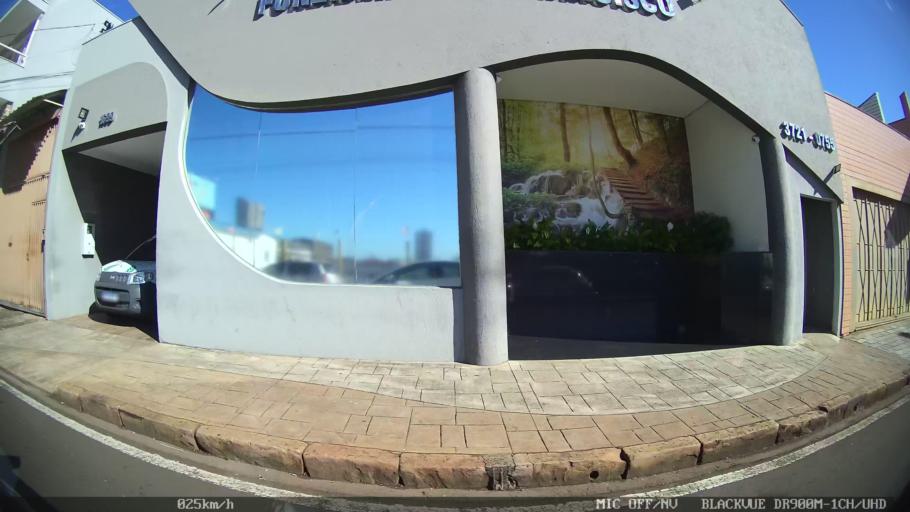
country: BR
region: Sao Paulo
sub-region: Franca
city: Franca
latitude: -20.5388
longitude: -47.3993
